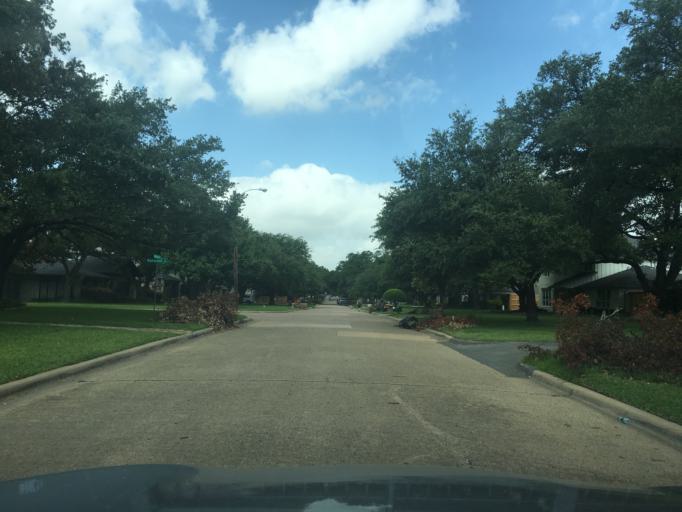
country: US
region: Texas
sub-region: Dallas County
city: Addison
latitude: 32.9120
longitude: -96.8260
